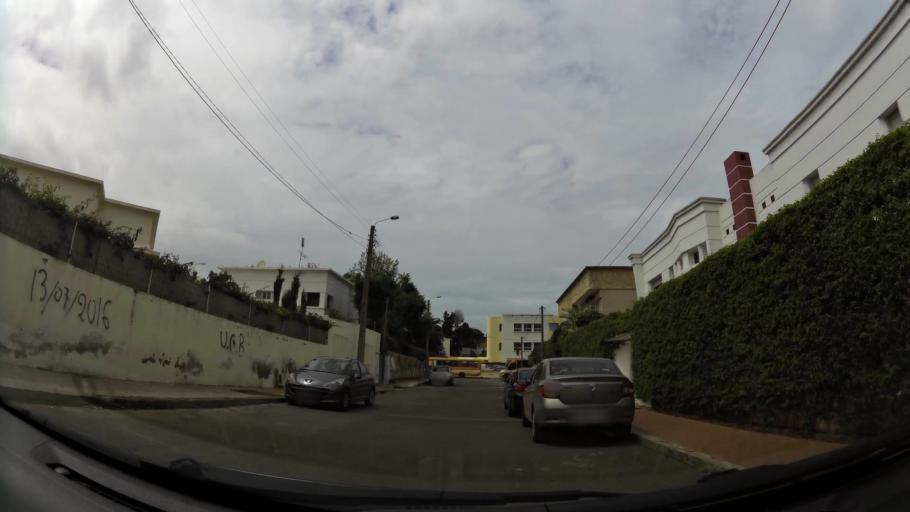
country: MA
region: Grand Casablanca
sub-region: Casablanca
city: Casablanca
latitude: 33.5624
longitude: -7.6369
